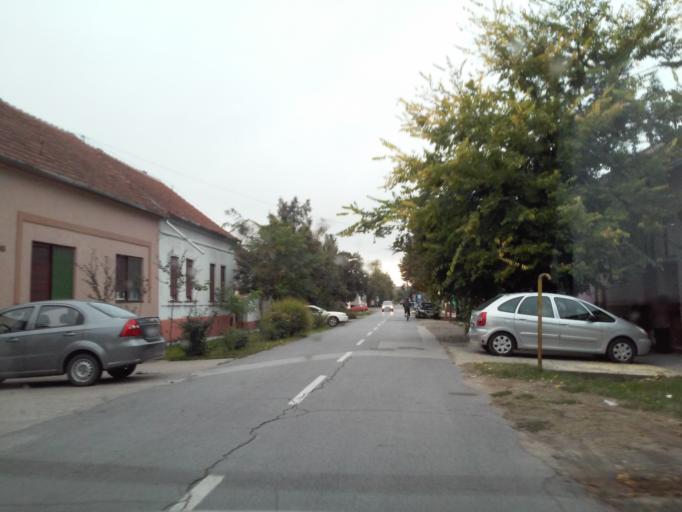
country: RS
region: Autonomna Pokrajina Vojvodina
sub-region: Severnobanatski Okrug
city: Kikinda
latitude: 45.8267
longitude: 20.4623
